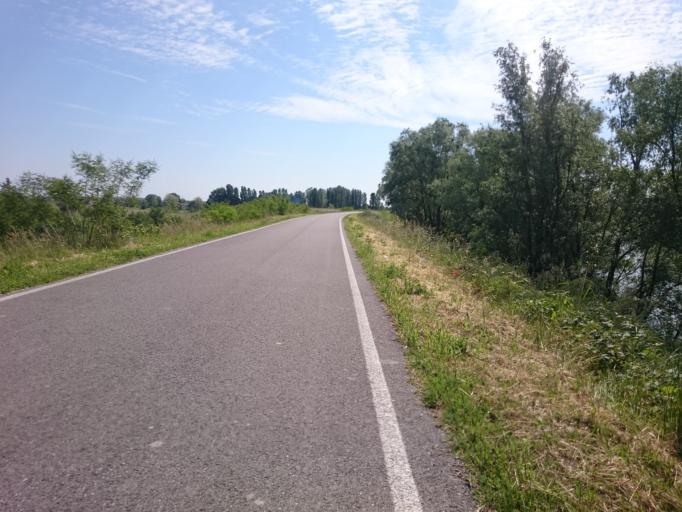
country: IT
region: Veneto
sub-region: Provincia di Rovigo
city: Corbola
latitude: 44.9719
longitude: 12.0957
